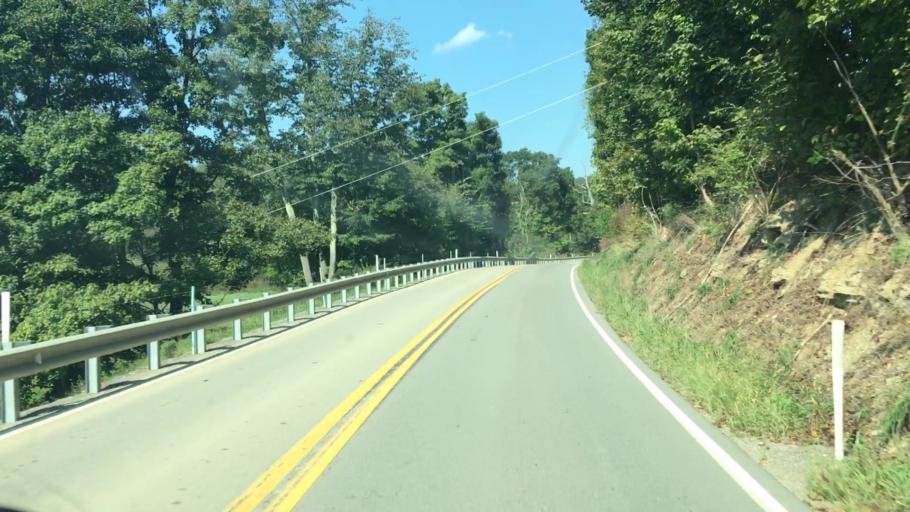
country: US
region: Pennsylvania
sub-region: Greene County
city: Waynesburg
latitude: 39.9664
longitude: -80.3156
